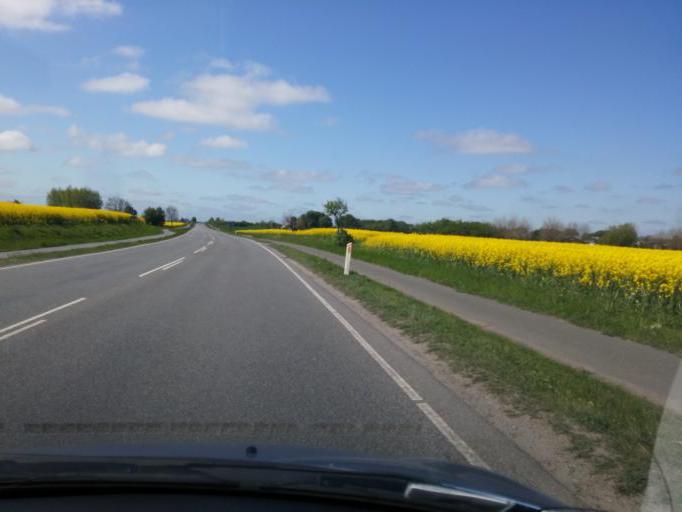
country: DK
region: South Denmark
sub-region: Kerteminde Kommune
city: Munkebo
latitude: 55.4507
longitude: 10.5366
